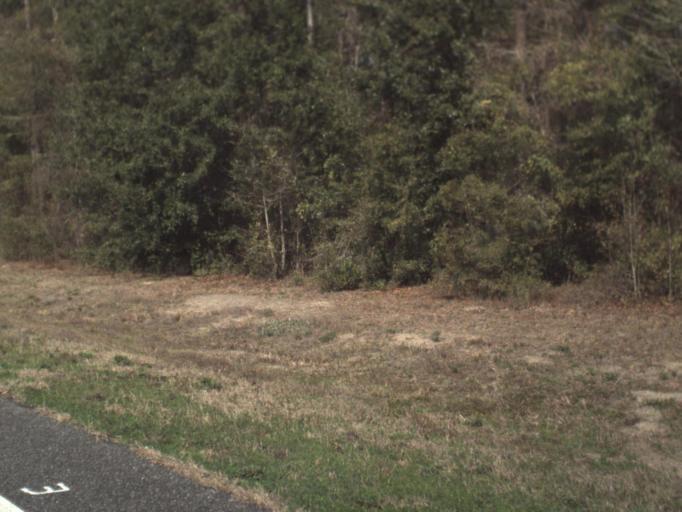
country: US
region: Florida
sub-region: Leon County
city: Woodville
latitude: 30.4198
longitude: -84.0959
